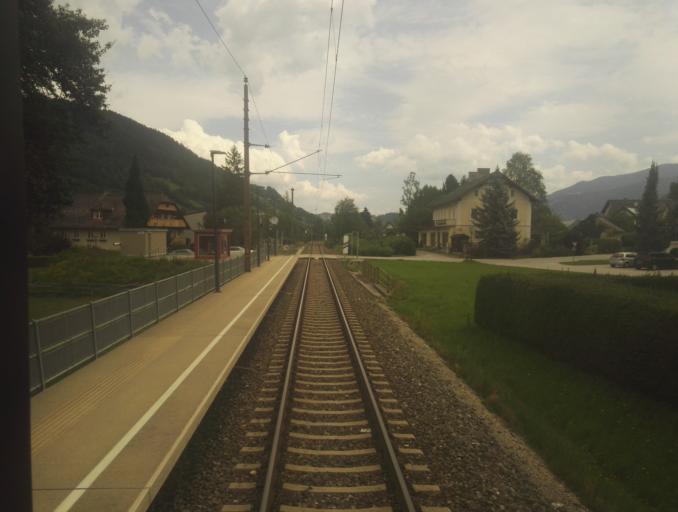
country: AT
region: Styria
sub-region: Politischer Bezirk Liezen
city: Pruggern
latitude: 47.4231
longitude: 13.8747
